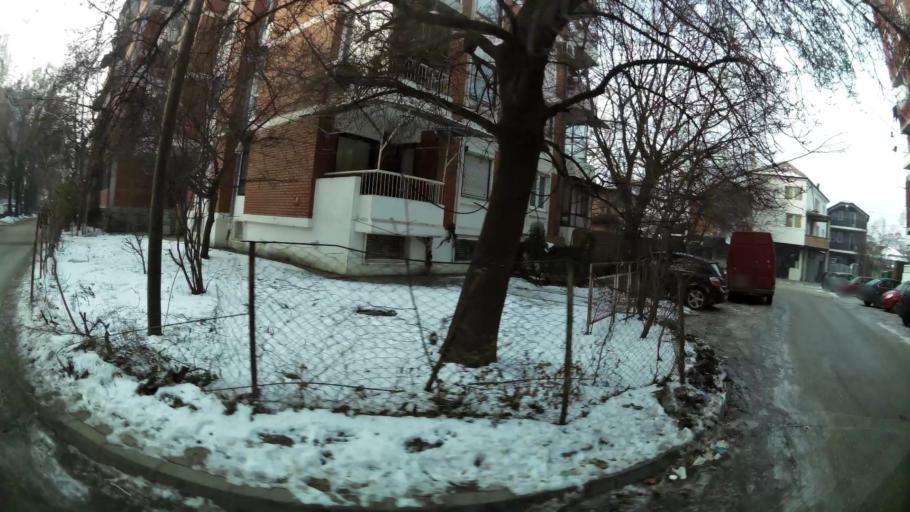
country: MK
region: Cair
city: Cair
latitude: 42.0186
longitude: 21.4398
